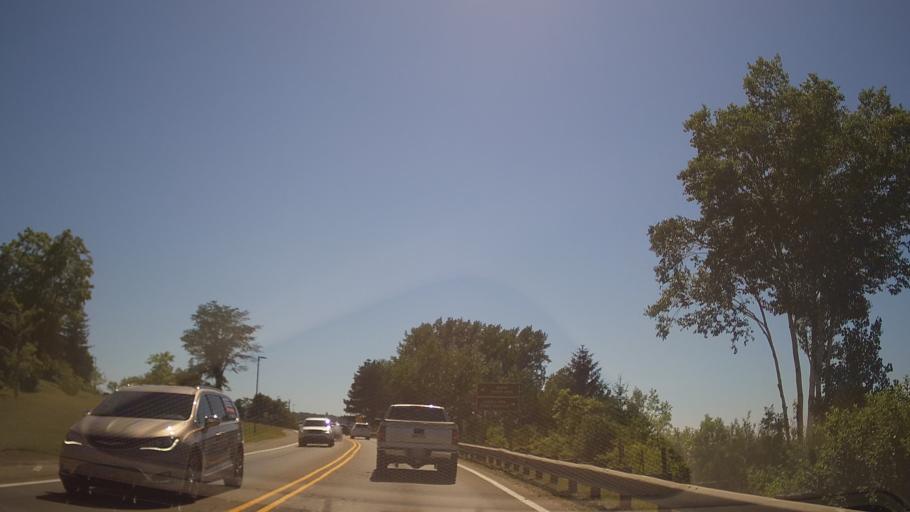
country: US
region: Michigan
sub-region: Emmet County
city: Petoskey
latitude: 45.3802
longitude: -84.9490
